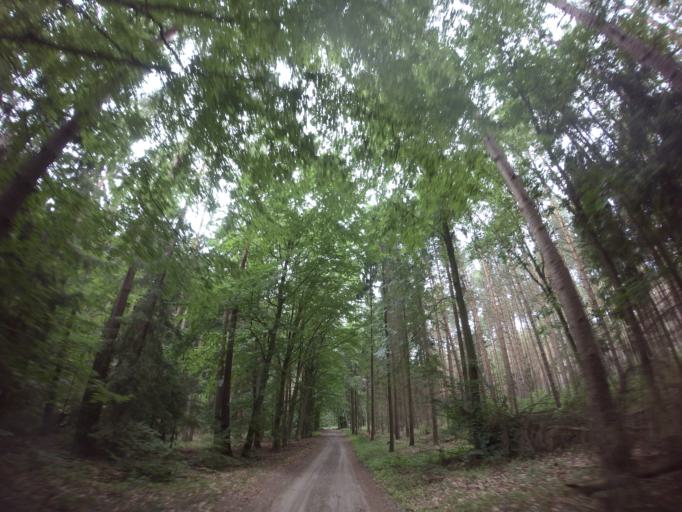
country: PL
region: Lubusz
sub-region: Powiat strzelecko-drezdenecki
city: Strzelce Krajenskie
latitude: 52.9321
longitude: 15.6103
